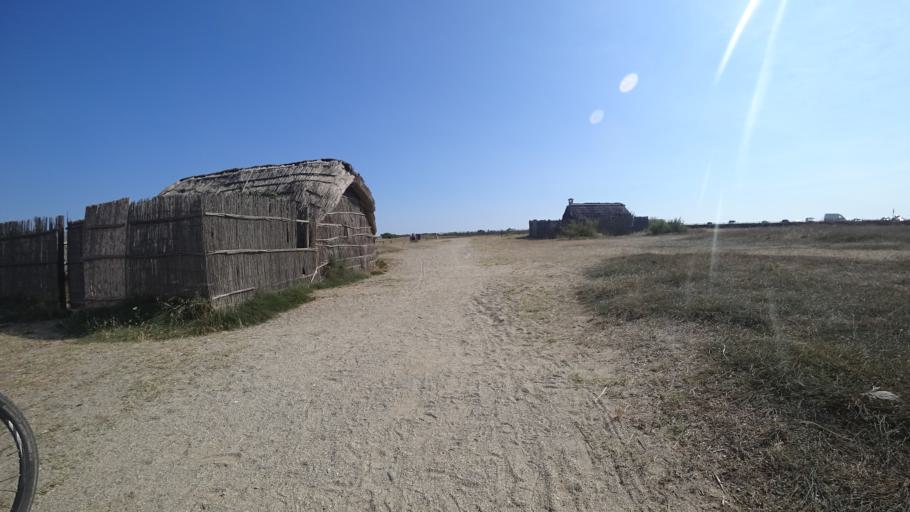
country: FR
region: Languedoc-Roussillon
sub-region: Departement des Pyrenees-Orientales
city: Saint-Cyprien-Plage
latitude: 42.6607
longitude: 3.0313
